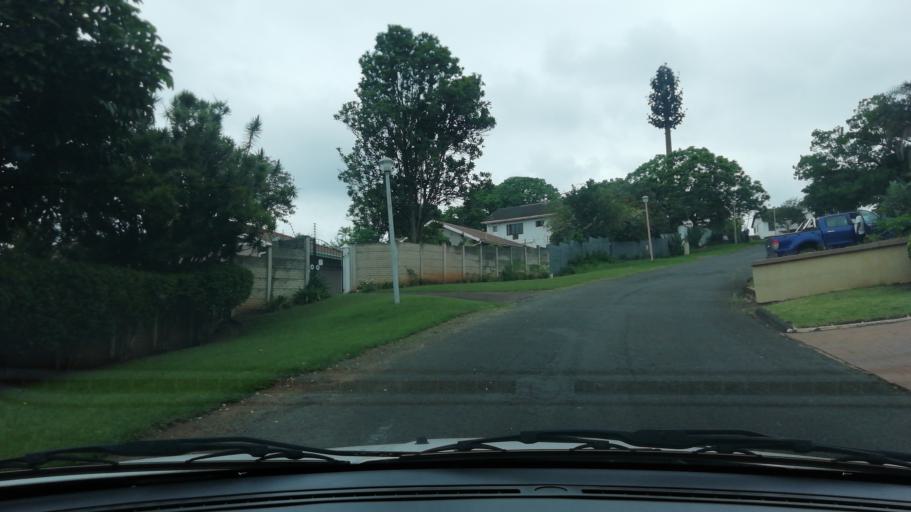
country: ZA
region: KwaZulu-Natal
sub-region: uThungulu District Municipality
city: Empangeni
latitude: -28.7583
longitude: 31.8889
